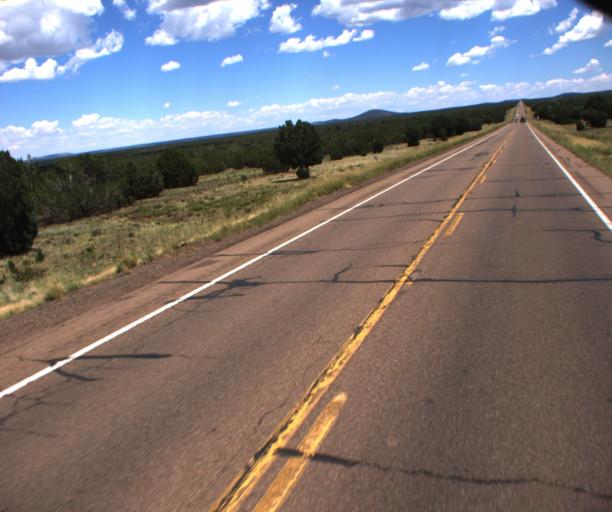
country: US
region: Arizona
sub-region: Navajo County
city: Show Low
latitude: 34.2647
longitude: -109.9584
